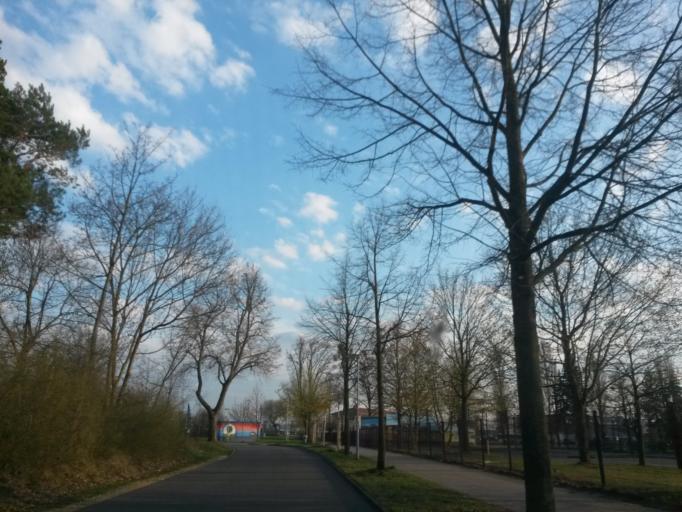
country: DE
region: Brandenburg
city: Strausberg
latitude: 52.5928
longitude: 13.9086
